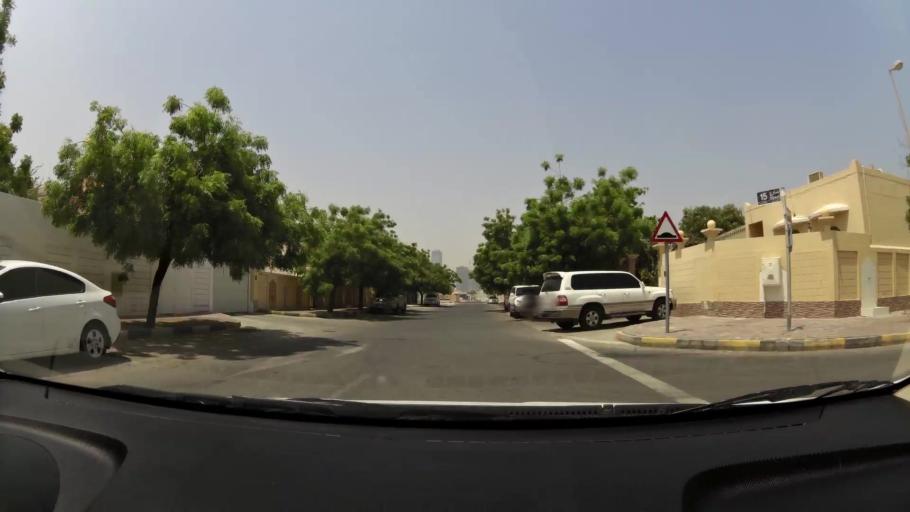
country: AE
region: Ash Shariqah
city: Sharjah
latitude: 25.3441
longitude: 55.3726
